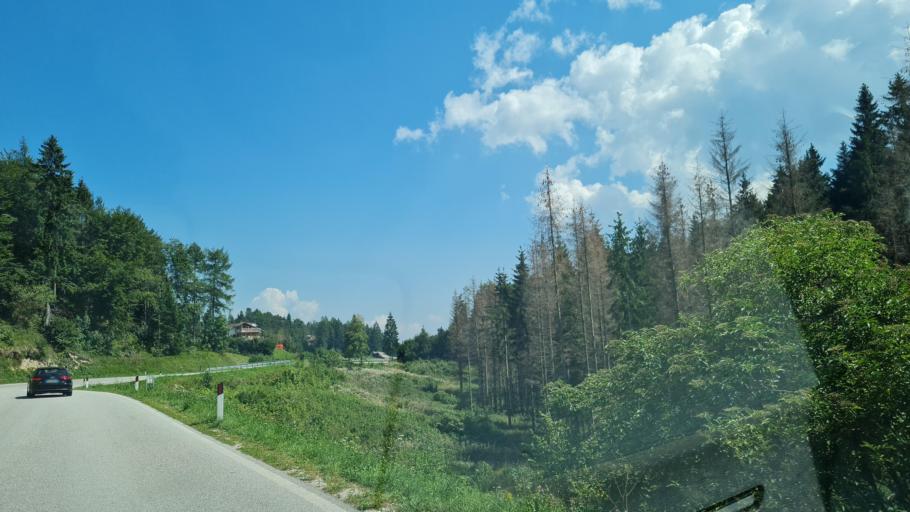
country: IT
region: Trentino-Alto Adige
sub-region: Provincia di Trento
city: Centa San Nicolo
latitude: 45.9479
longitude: 11.2441
